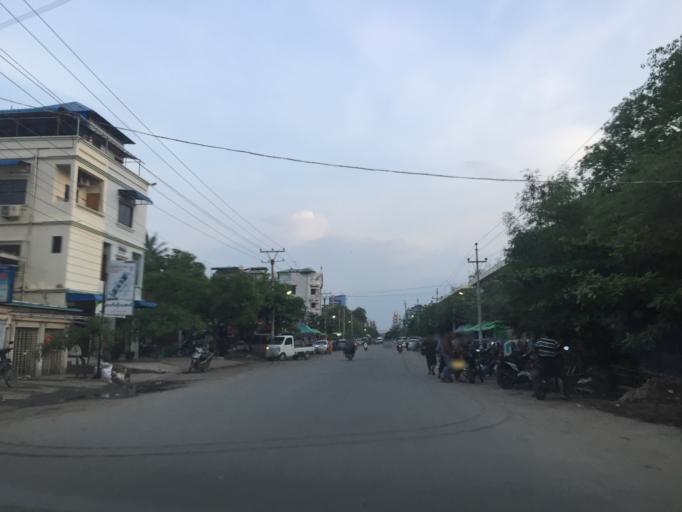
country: MM
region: Mandalay
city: Mandalay
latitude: 21.9798
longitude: 96.0887
